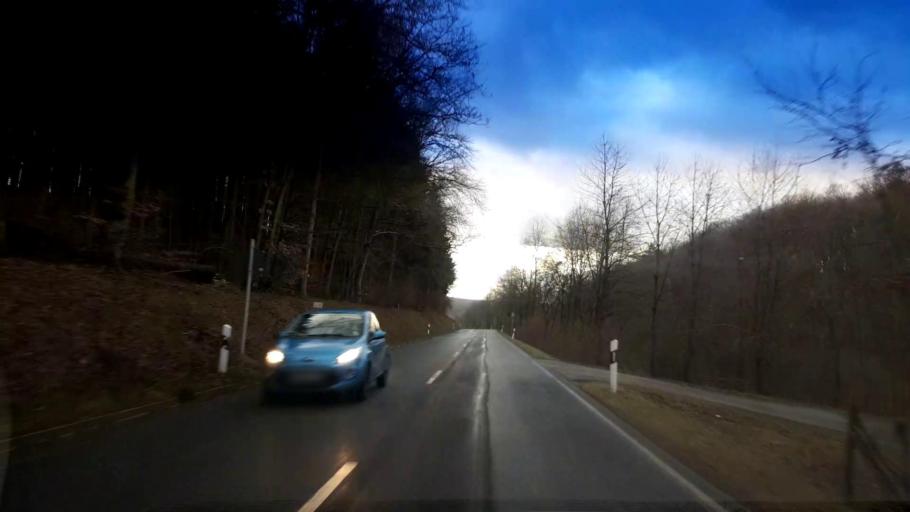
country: DE
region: Bavaria
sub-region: Upper Franconia
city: Lauter
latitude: 49.9692
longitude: 10.7565
